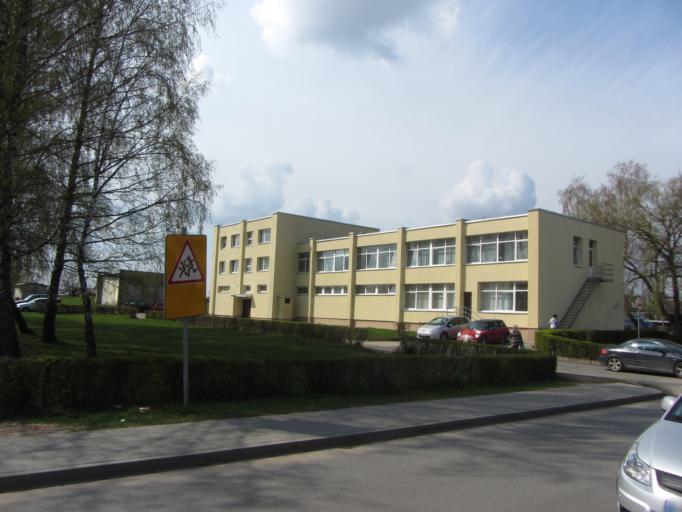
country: LT
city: Lentvaris
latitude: 54.6405
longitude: 25.0446
